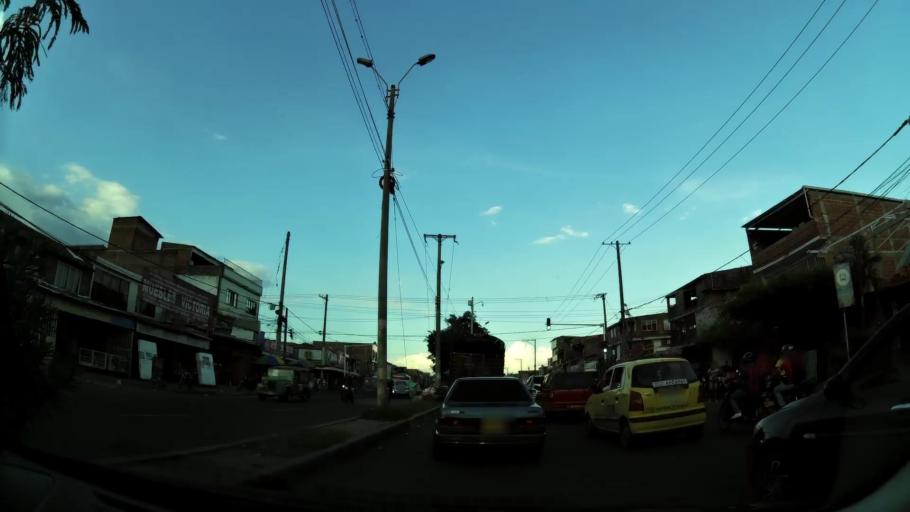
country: CO
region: Valle del Cauca
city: Cali
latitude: 3.4104
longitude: -76.4935
